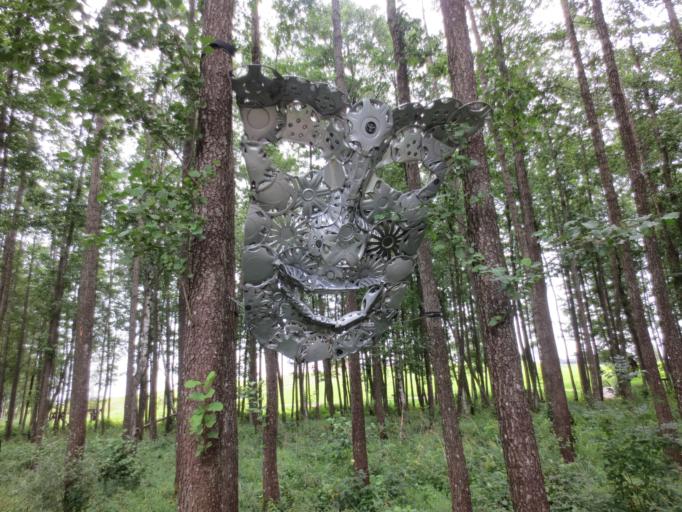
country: LT
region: Utenos apskritis
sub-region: Anyksciai
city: Anyksciai
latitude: 55.4930
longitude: 25.2399
